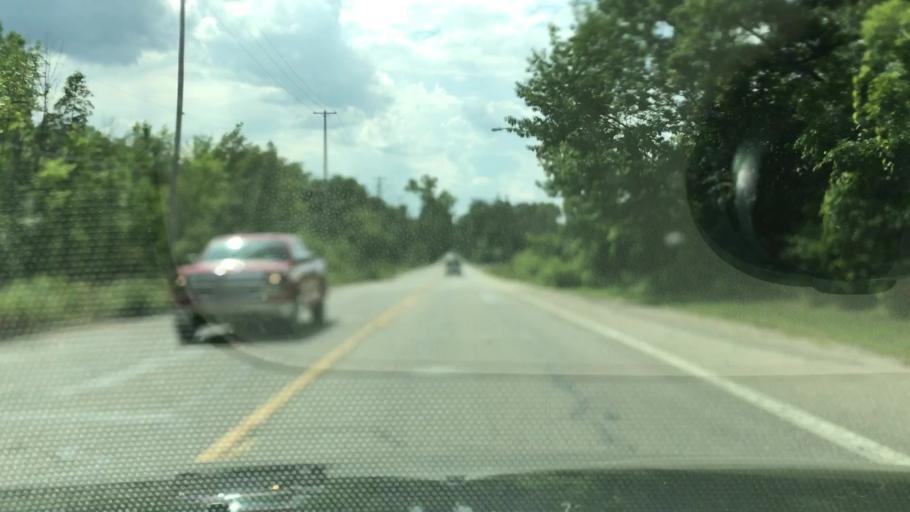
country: US
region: Michigan
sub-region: Kent County
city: East Grand Rapids
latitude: 42.9700
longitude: -85.6009
